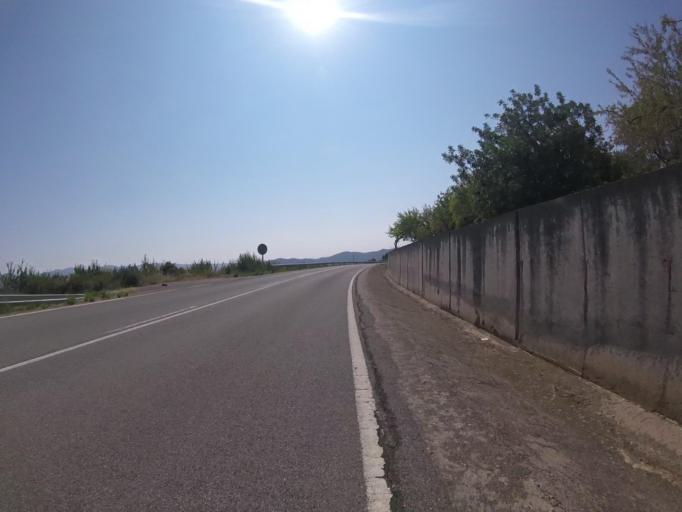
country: ES
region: Valencia
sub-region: Provincia de Castello
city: Adzaneta
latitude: 40.2438
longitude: -0.1928
